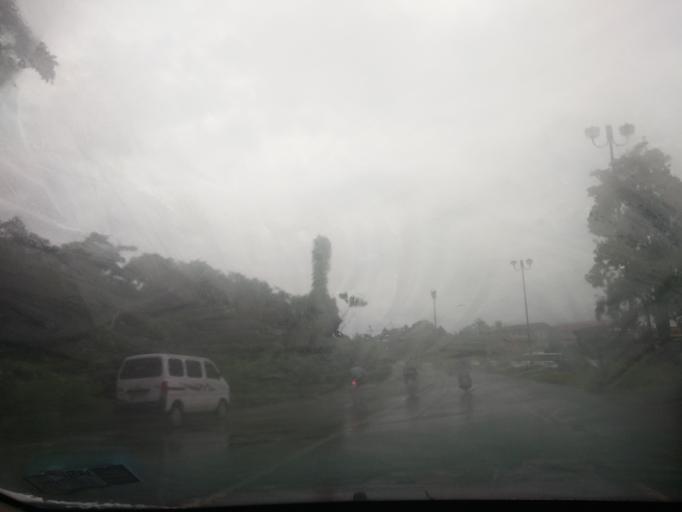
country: IN
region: Goa
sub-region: North Goa
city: Panaji
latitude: 15.5160
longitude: 73.8344
